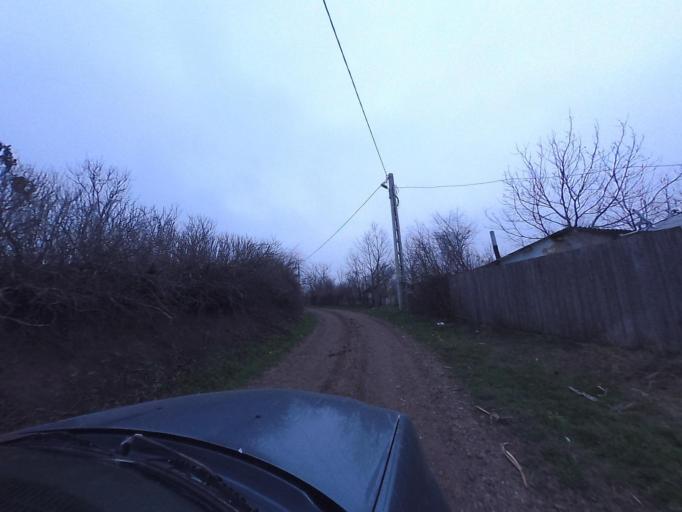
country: RO
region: Vaslui
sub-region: Comuna Vinderei
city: Vinderei
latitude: 46.1439
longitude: 27.7481
